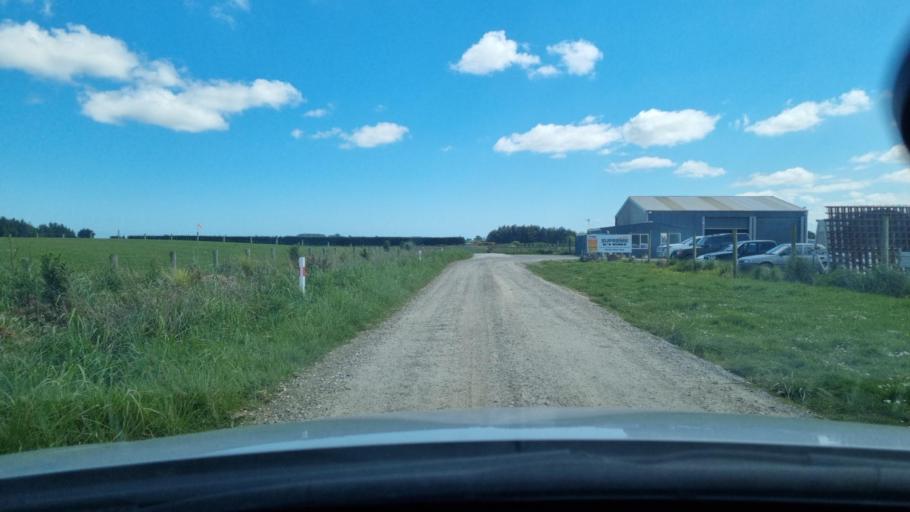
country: NZ
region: Southland
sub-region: Invercargill City
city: Invercargill
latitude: -46.3740
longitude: 168.3388
